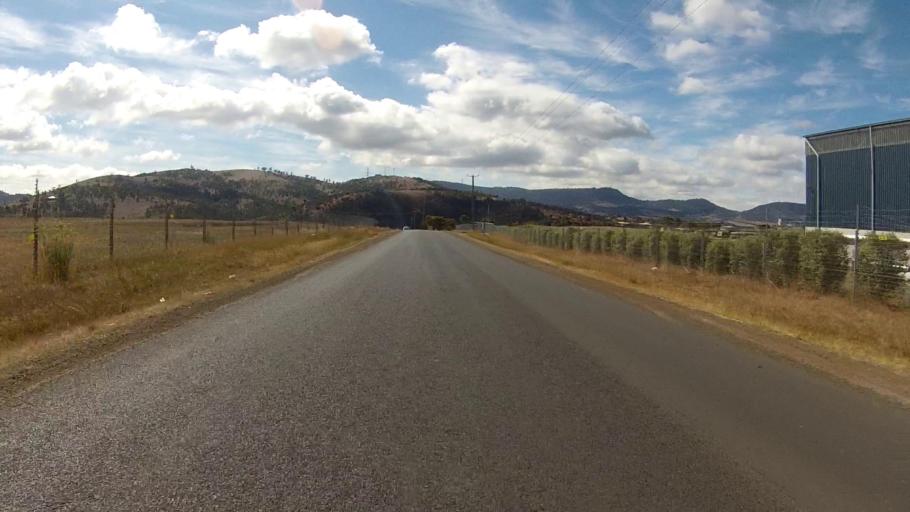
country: AU
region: Tasmania
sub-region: Brighton
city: Bridgewater
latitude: -42.7357
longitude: 147.2530
